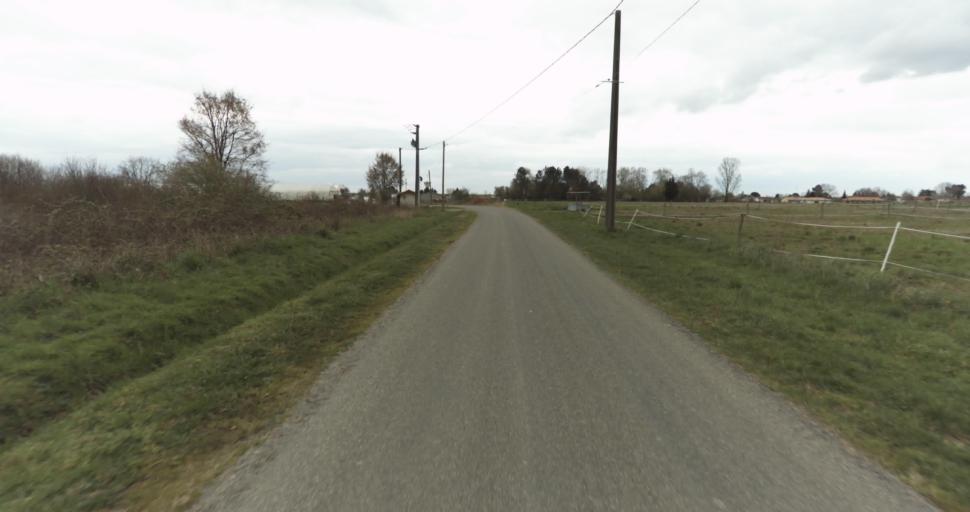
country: FR
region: Aquitaine
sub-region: Departement des Landes
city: Roquefort
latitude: 44.0206
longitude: -0.3312
